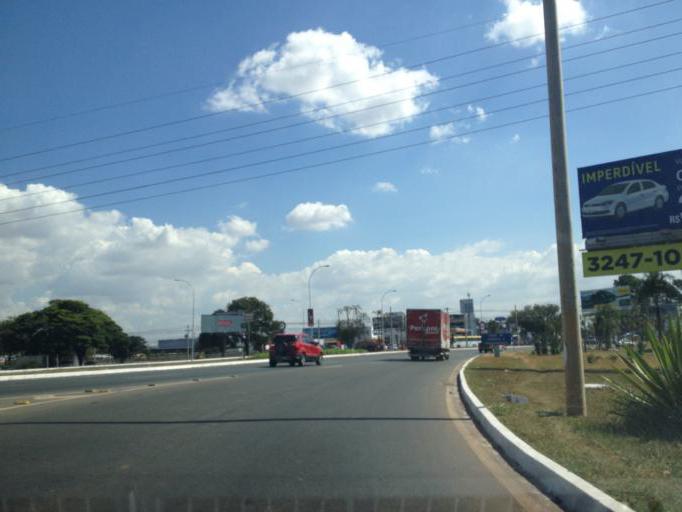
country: BR
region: Federal District
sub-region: Brasilia
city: Brasilia
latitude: -15.8075
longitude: -47.9498
